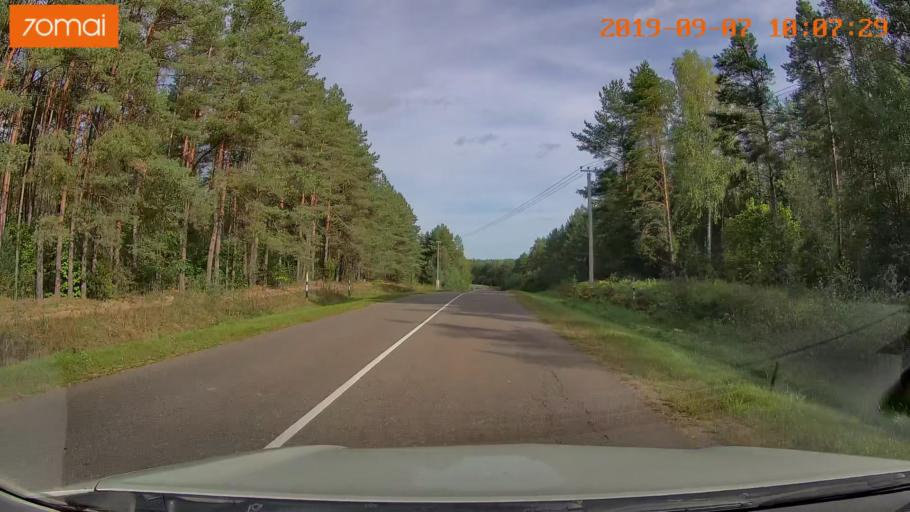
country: BY
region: Grodnenskaya
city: Voranava
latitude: 54.0760
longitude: 25.3963
